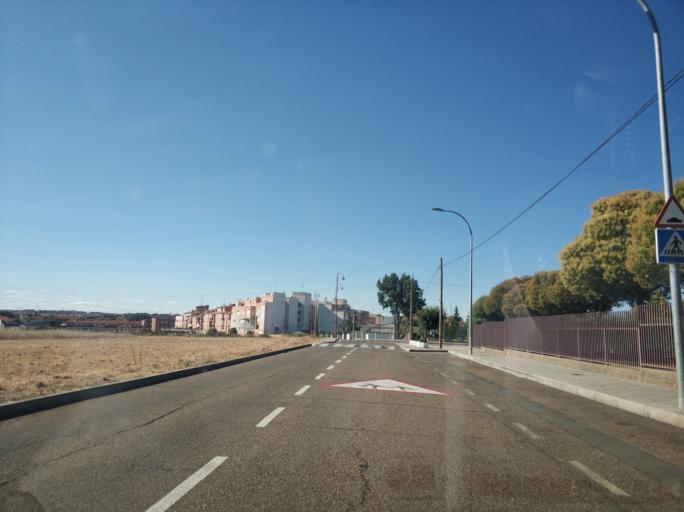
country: ES
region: Castille and Leon
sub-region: Provincia de Salamanca
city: Santa Marta de Tormes
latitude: 40.9468
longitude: -5.6275
